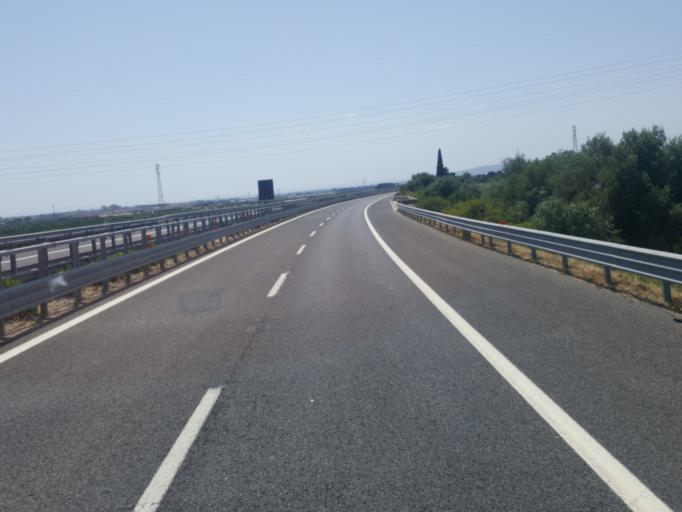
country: IT
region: Apulia
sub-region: Provincia di Taranto
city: Palagiano
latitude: 40.5936
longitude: 17.0721
